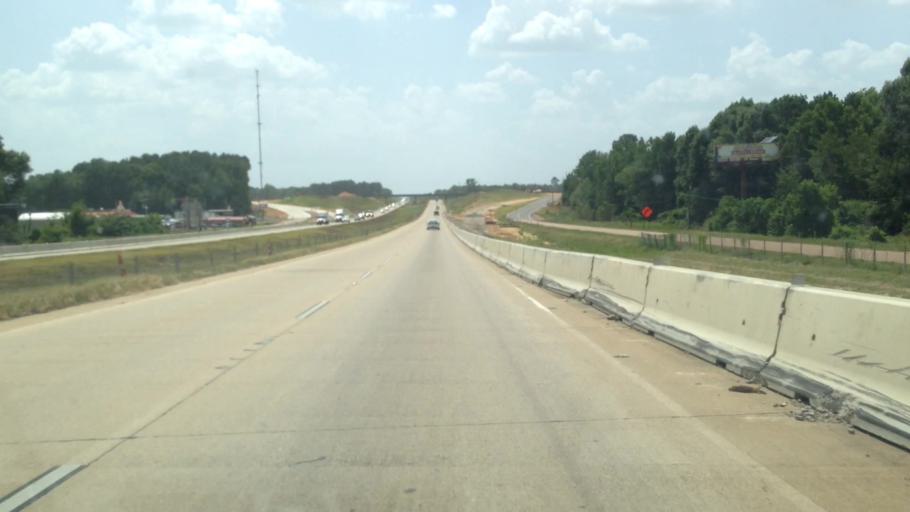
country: US
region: Louisiana
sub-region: Lincoln Parish
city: Ruston
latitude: 32.5404
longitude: -92.6697
